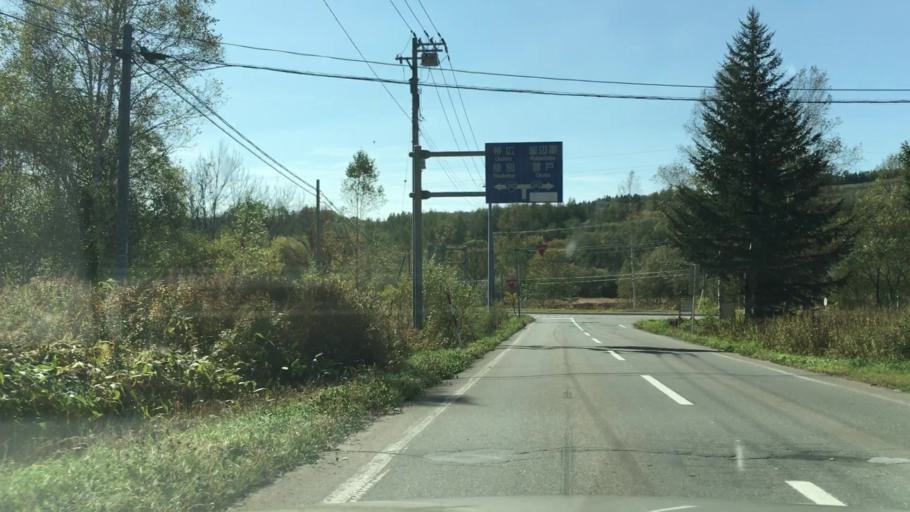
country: JP
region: Hokkaido
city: Kitami
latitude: 43.5846
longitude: 143.6820
